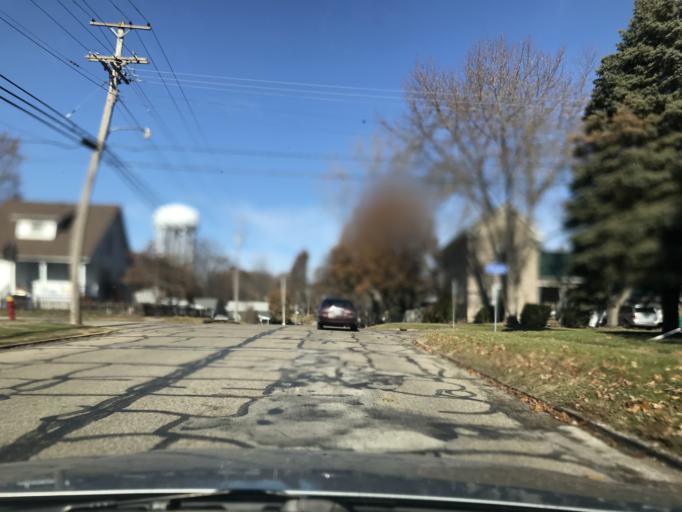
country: US
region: Illinois
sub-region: McDonough County
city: Macomb
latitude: 40.4506
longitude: -90.6673
